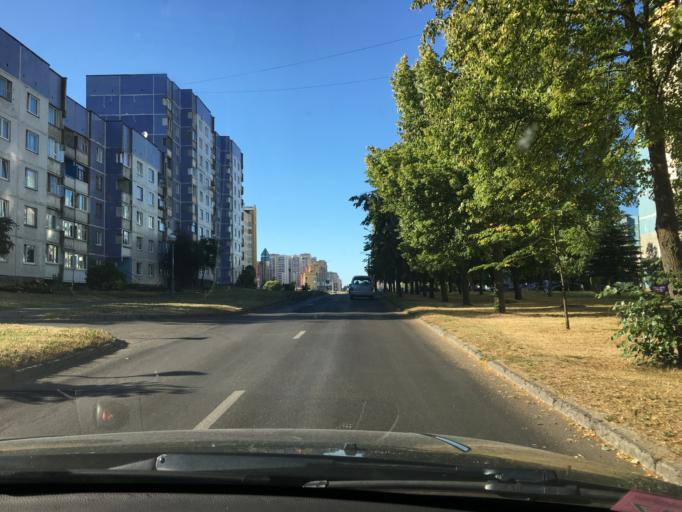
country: BY
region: Grodnenskaya
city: Hrodna
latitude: 53.7043
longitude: 23.8496
